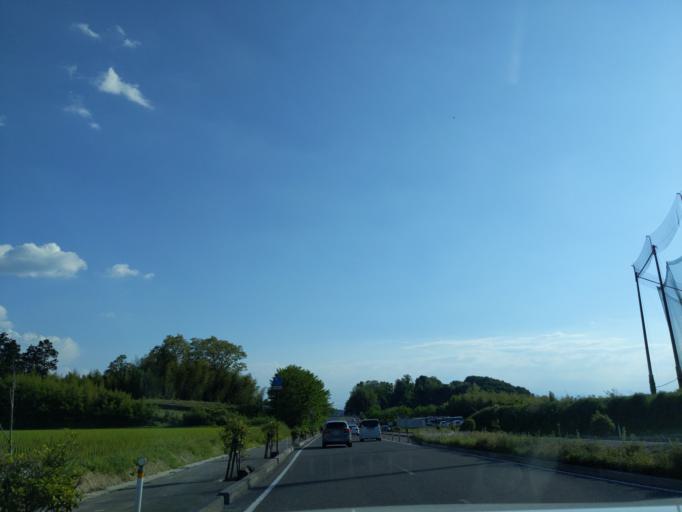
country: JP
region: Fukushima
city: Sukagawa
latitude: 37.2800
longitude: 140.3804
